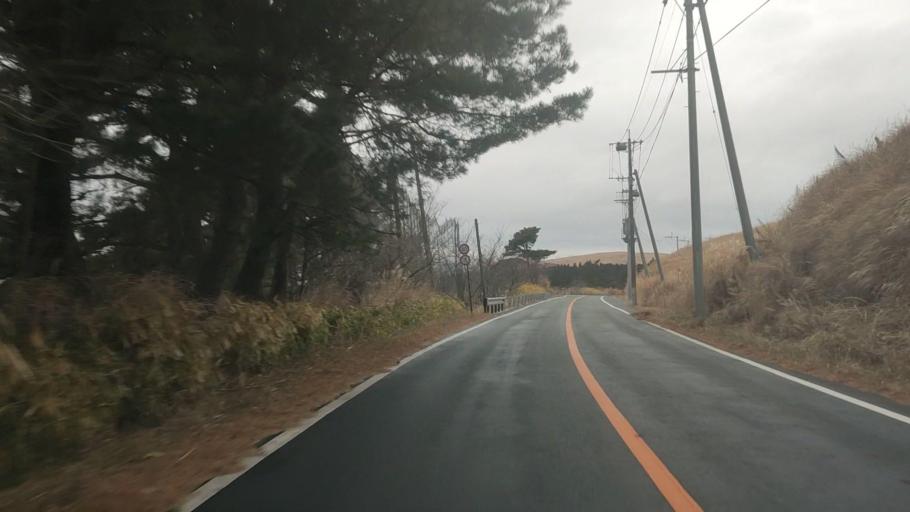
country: JP
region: Kumamoto
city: Aso
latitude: 32.8936
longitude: 131.0271
